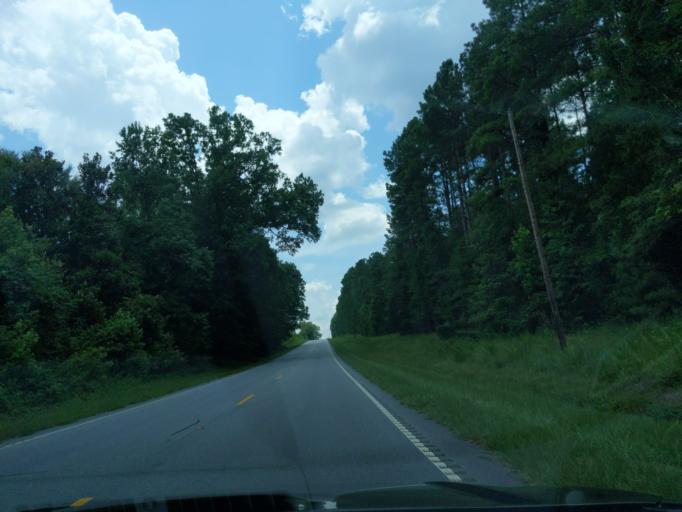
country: US
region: South Carolina
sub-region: Greenwood County
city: Ninety Six
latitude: 34.0235
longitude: -82.0404
